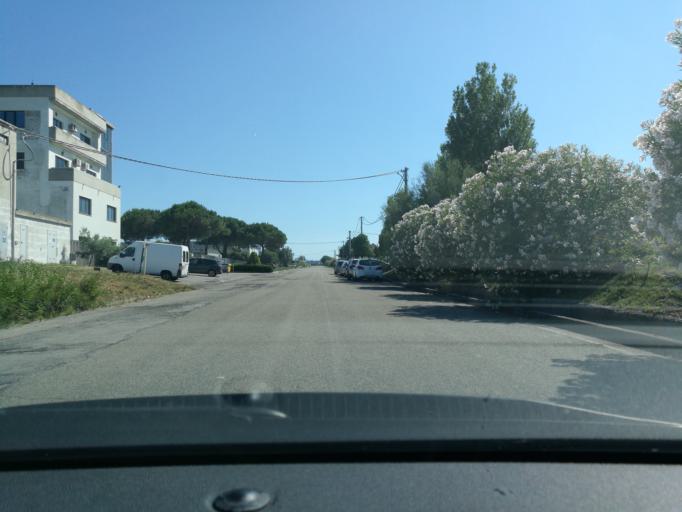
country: IT
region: Abruzzo
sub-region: Provincia di Chieti
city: Vasto
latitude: 42.1727
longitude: 14.6974
